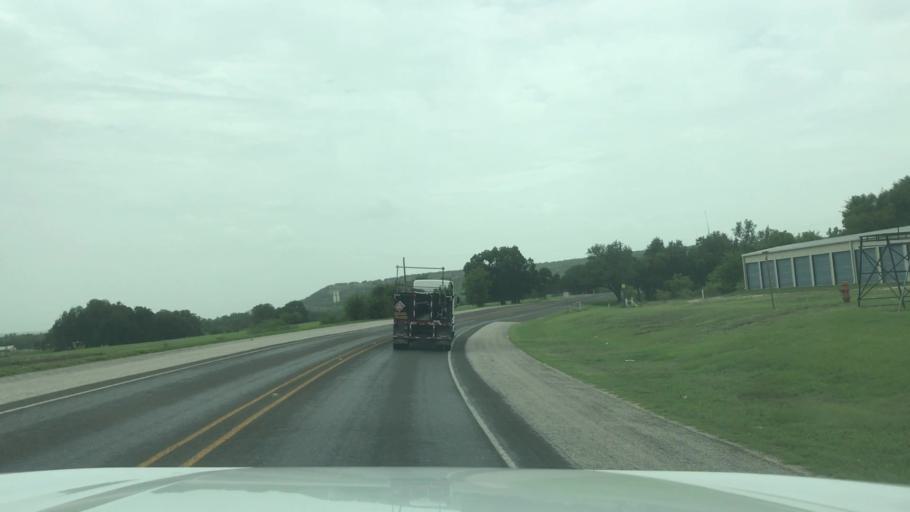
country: US
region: Texas
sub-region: Bosque County
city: Meridian
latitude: 31.9129
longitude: -97.6619
